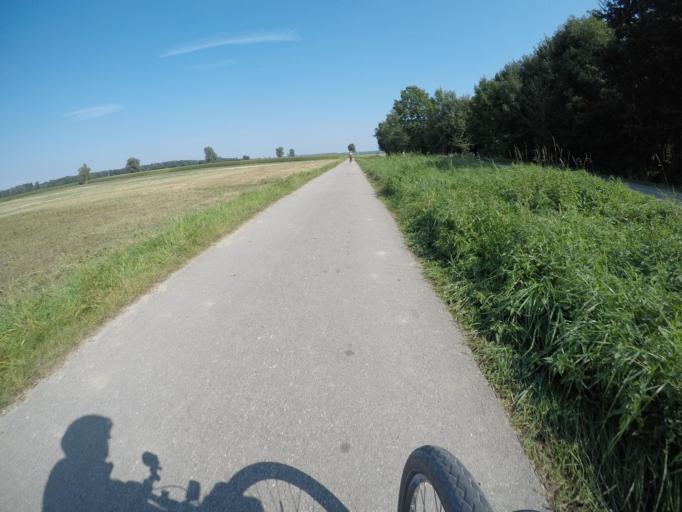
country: DE
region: Bavaria
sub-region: Swabia
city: Zusamaltheim
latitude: 48.5411
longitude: 10.6049
